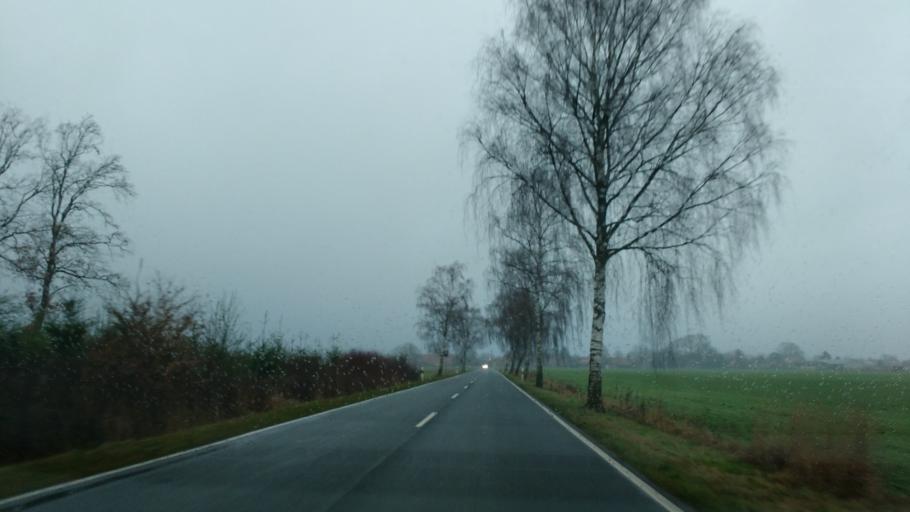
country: DE
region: Lower Saxony
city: Gilten
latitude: 52.6753
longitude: 9.5734
